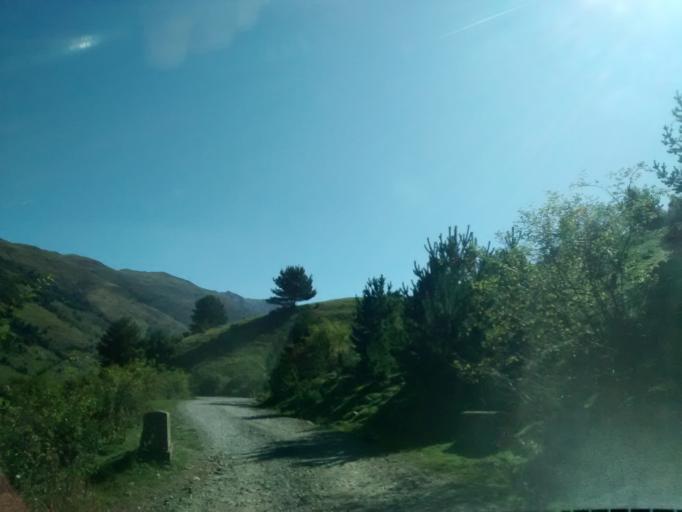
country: ES
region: Aragon
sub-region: Provincia de Huesca
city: Aragues del Puerto
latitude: 42.8529
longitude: -0.6952
